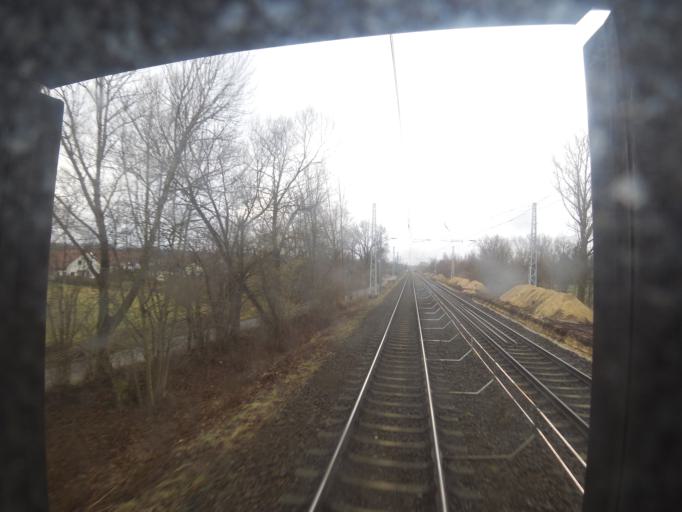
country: DE
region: Brandenburg
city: Rangsdorf
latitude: 52.2880
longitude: 13.4330
